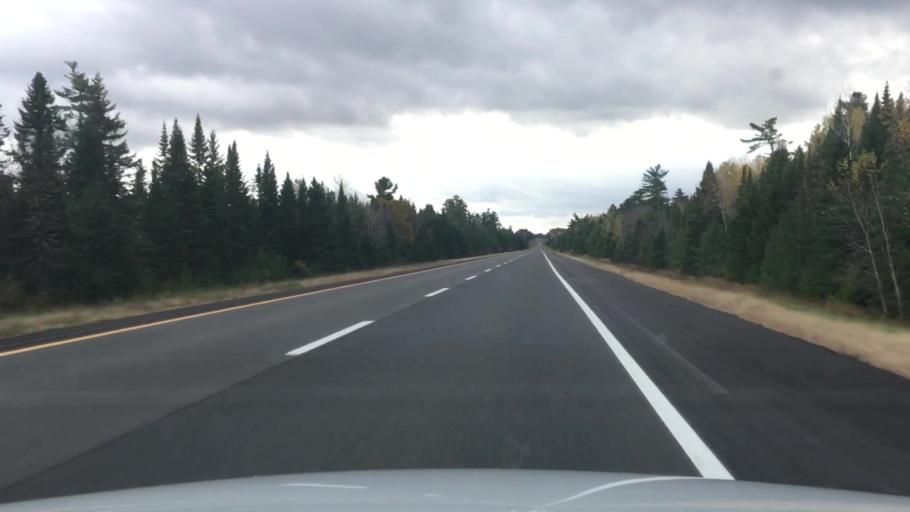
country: US
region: Maine
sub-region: Penobscot County
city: Patten
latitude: 46.0757
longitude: -68.2190
